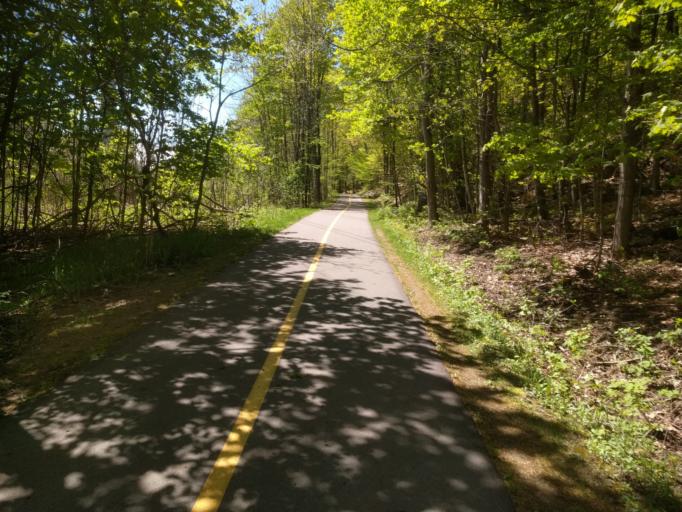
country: CA
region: Quebec
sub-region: Outaouais
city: Gatineau
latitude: 45.4760
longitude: -75.7928
